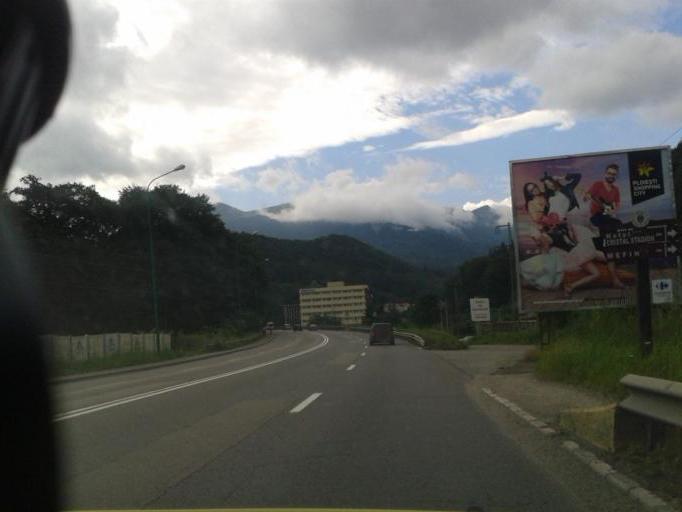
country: RO
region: Prahova
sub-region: Oras Sinaia
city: Sinaia
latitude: 45.3322
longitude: 25.5608
